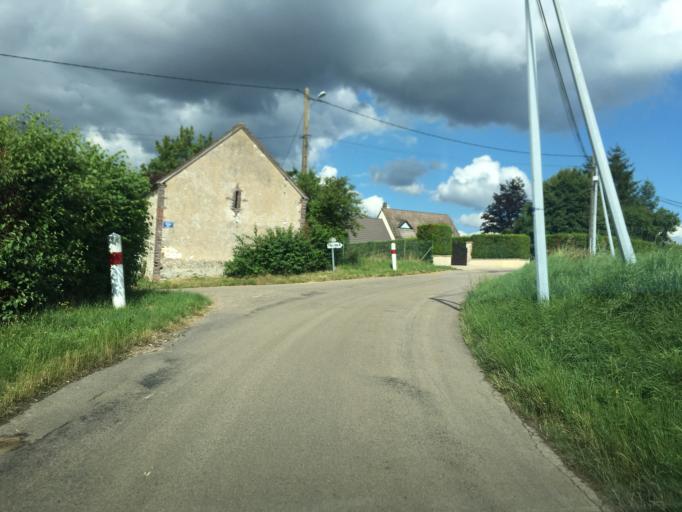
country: FR
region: Bourgogne
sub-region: Departement de l'Yonne
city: Aillant-sur-Tholon
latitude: 47.8225
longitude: 3.3891
